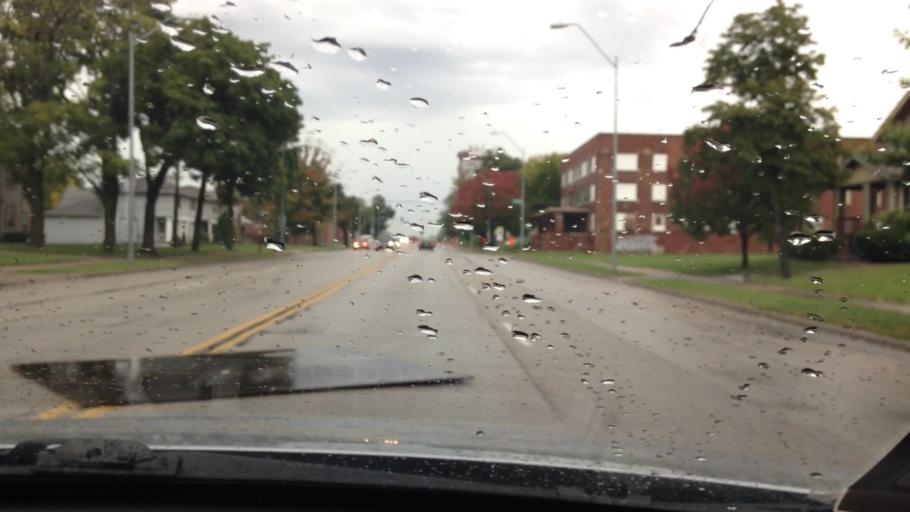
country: US
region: Missouri
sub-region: Jackson County
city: Kansas City
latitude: 39.0659
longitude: -94.5670
